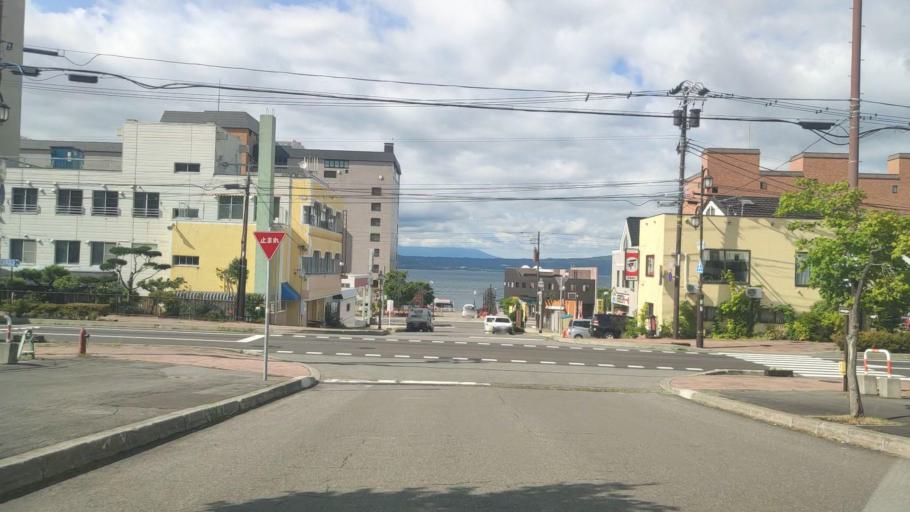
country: JP
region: Hokkaido
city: Date
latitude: 42.5645
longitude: 140.8230
